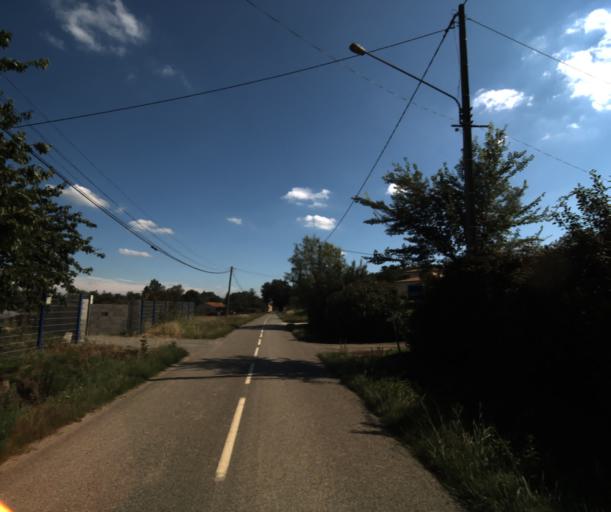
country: FR
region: Midi-Pyrenees
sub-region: Departement de la Haute-Garonne
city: Fonsorbes
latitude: 43.5090
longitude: 1.2191
